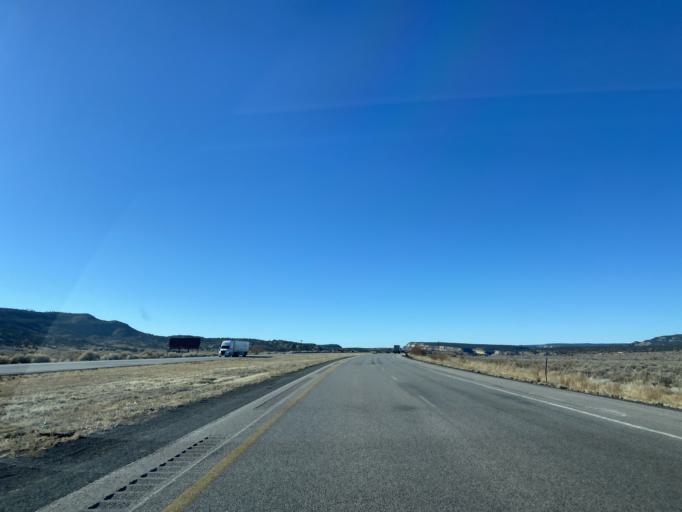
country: US
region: New Mexico
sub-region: McKinley County
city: Gallup
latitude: 35.4414
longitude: -108.9599
